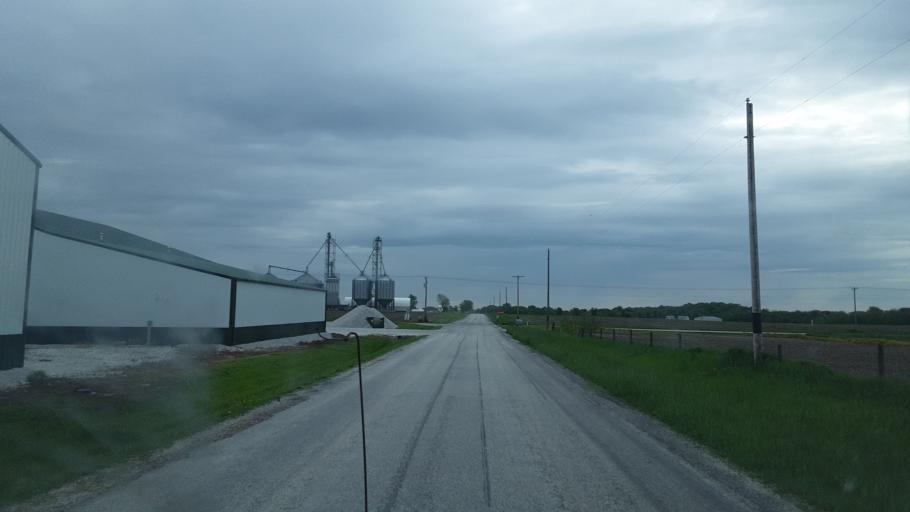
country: US
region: Illinois
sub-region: McDonough County
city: Macomb
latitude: 40.3816
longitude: -90.6208
